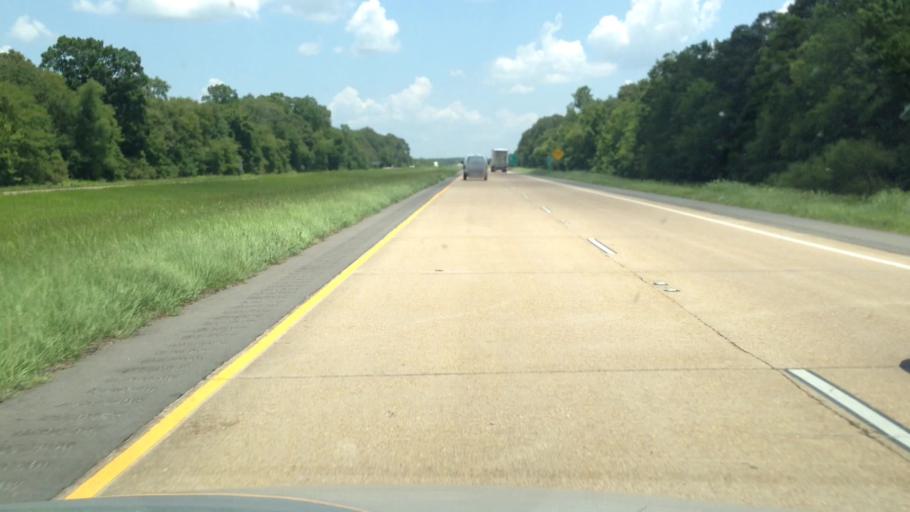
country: US
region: Louisiana
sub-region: Rapides Parish
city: Lecompte
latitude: 30.9947
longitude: -92.3261
